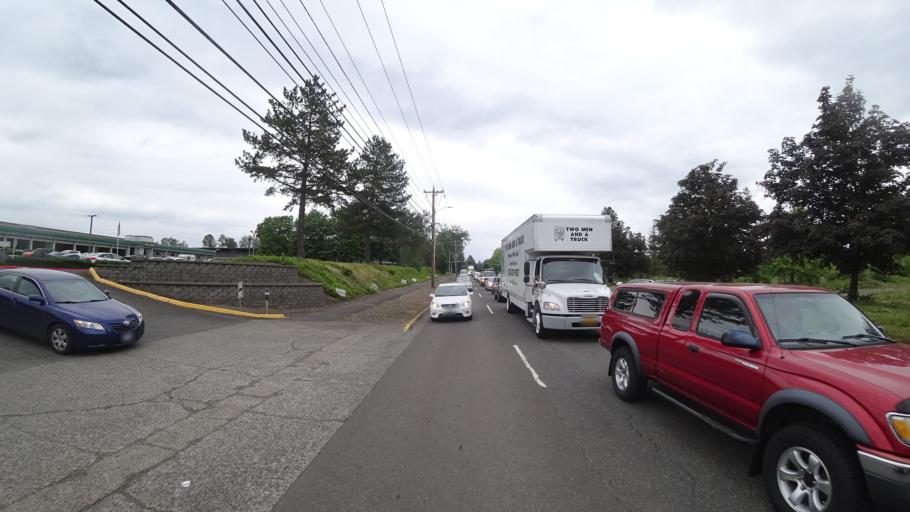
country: US
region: Oregon
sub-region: Washington County
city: Beaverton
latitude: 45.4767
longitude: -122.7867
